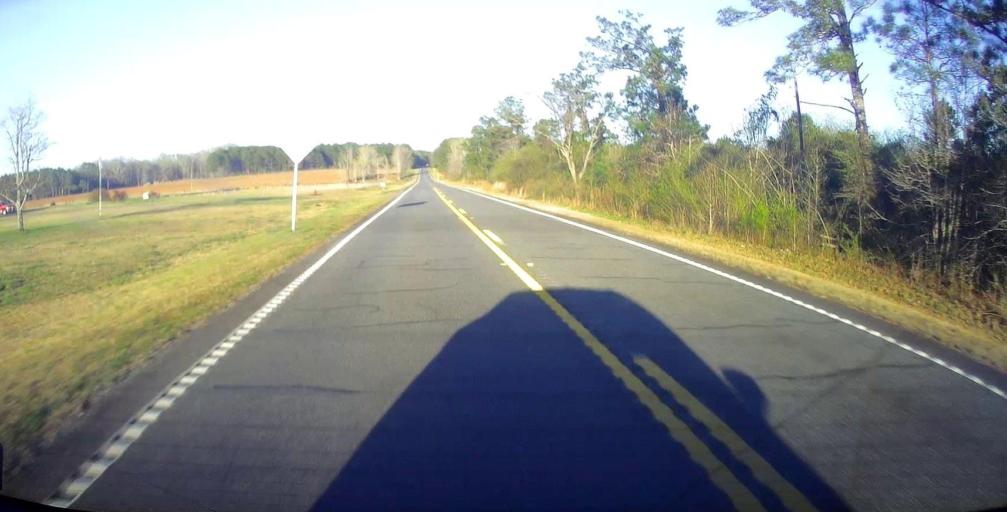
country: US
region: Georgia
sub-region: Talbot County
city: Talbotton
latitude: 32.6557
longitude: -84.6663
